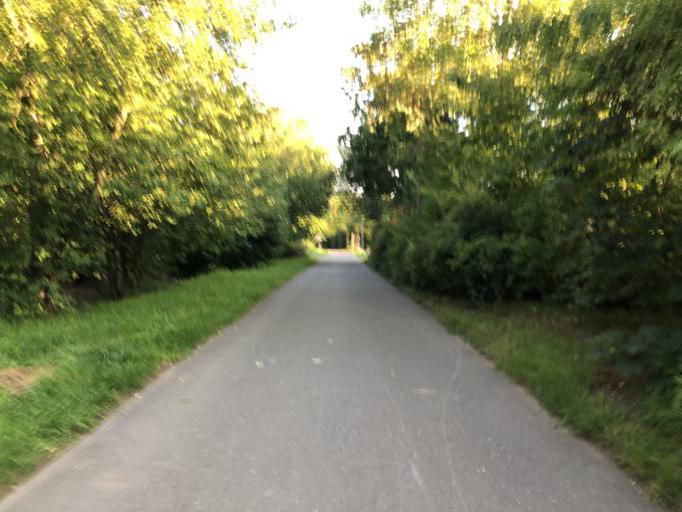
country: DE
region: Bavaria
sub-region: Regierungsbezirk Mittelfranken
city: Erlangen
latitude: 49.5938
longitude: 10.9554
